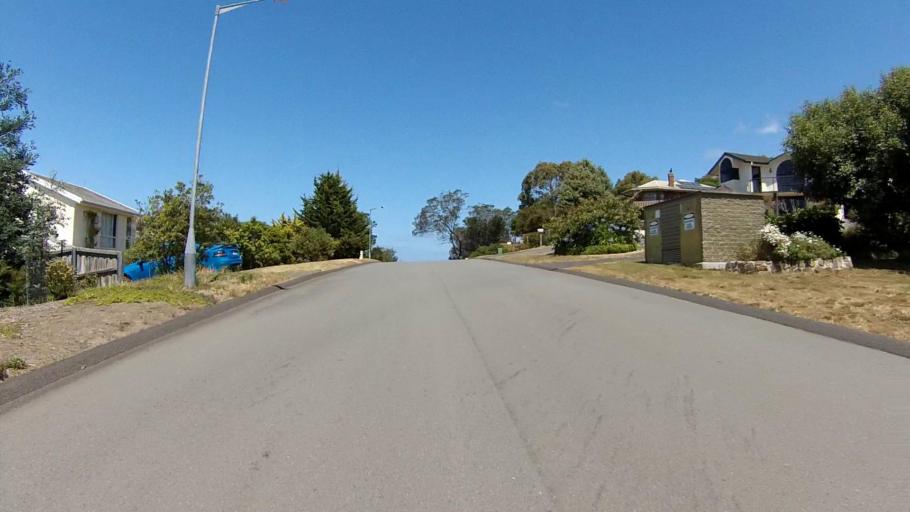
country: AU
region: Tasmania
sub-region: Clarence
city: Sandford
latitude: -42.9179
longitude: 147.5114
